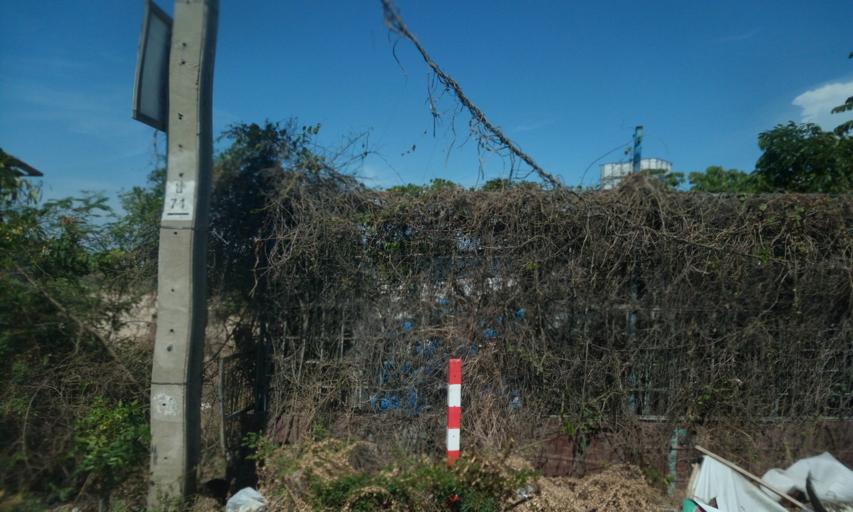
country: TH
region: Samut Prakan
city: Bang Bo District
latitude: 13.5376
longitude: 100.7882
